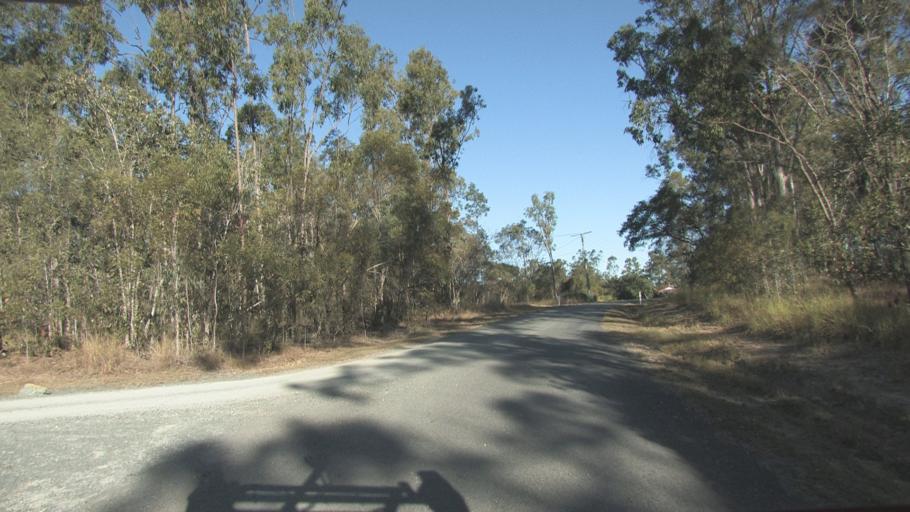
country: AU
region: Queensland
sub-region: Logan
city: North Maclean
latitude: -27.8090
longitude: 153.0495
